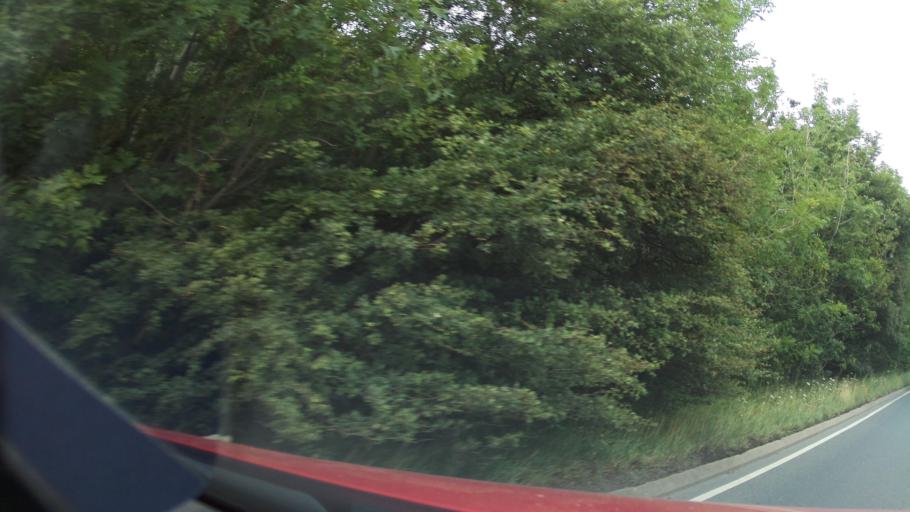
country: GB
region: England
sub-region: Northamptonshire
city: Geddington
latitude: 52.4489
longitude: -0.7358
